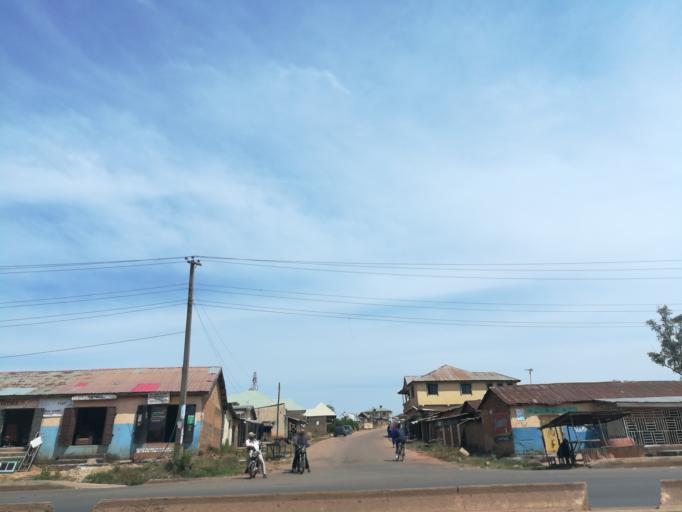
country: NG
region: Plateau
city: Bukuru
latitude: 9.7955
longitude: 8.8596
